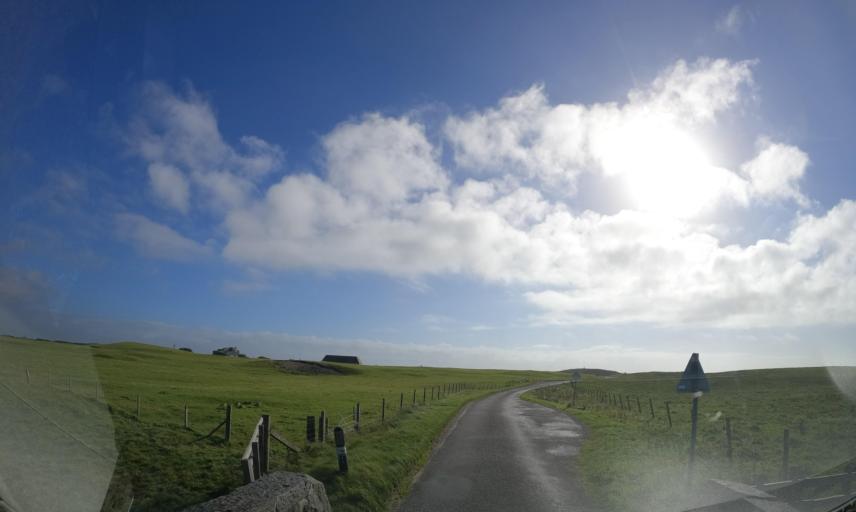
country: GB
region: Scotland
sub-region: Eilean Siar
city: Barra
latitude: 56.4933
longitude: -6.8475
